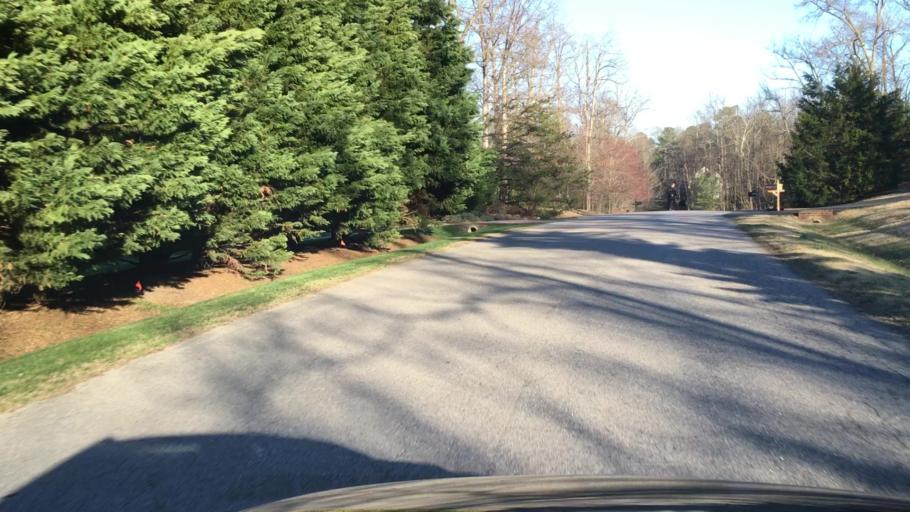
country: US
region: Virginia
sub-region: Chesterfield County
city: Bon Air
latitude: 37.5332
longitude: -77.6124
